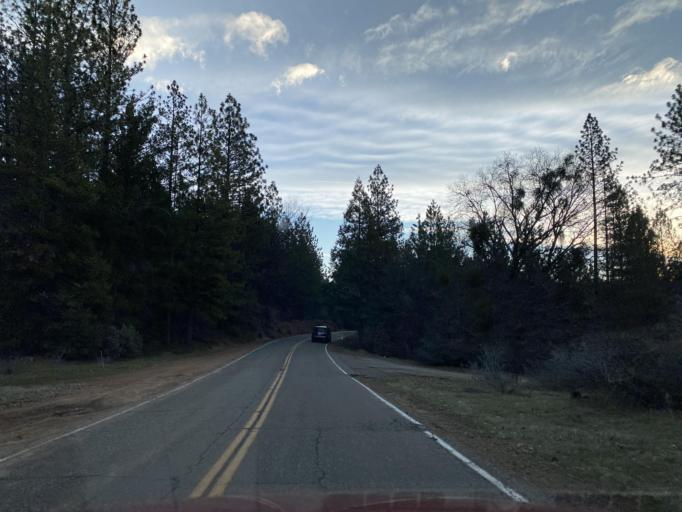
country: US
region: California
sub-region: Amador County
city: Pioneer
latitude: 38.4982
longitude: -120.6058
